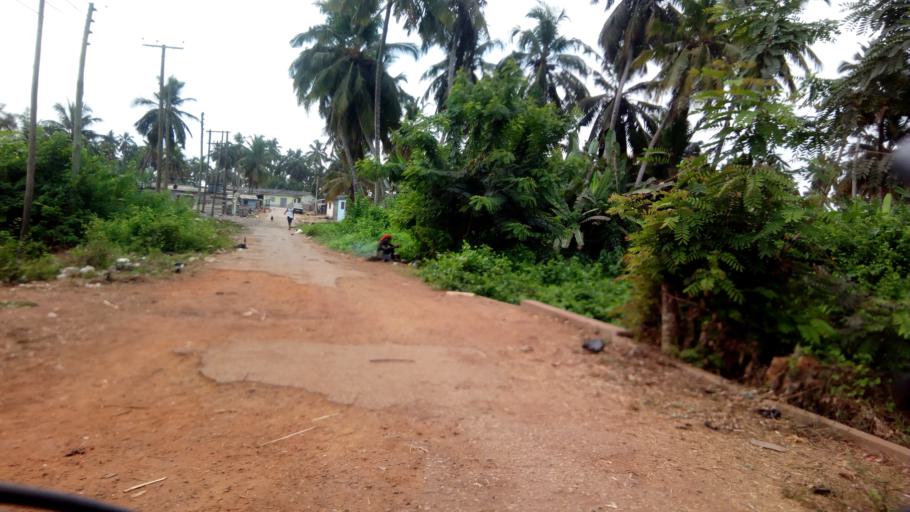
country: GH
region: Central
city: Cape Coast
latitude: 5.1023
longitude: -1.2807
